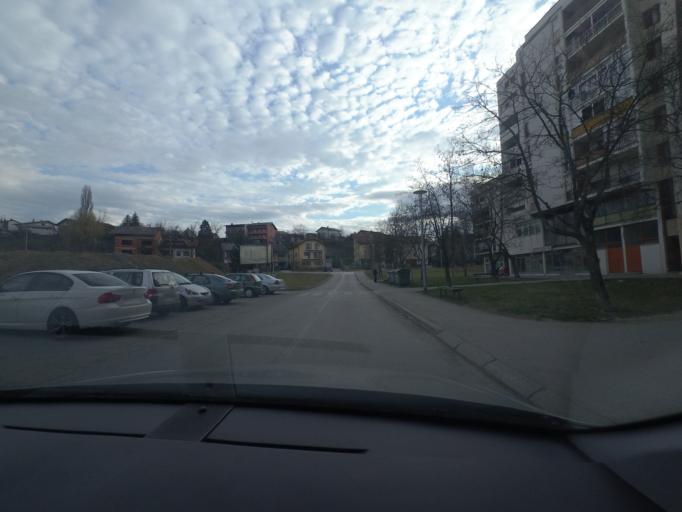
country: HR
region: Karlovacka
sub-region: Grad Karlovac
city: Karlovac
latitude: 45.4804
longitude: 15.5499
